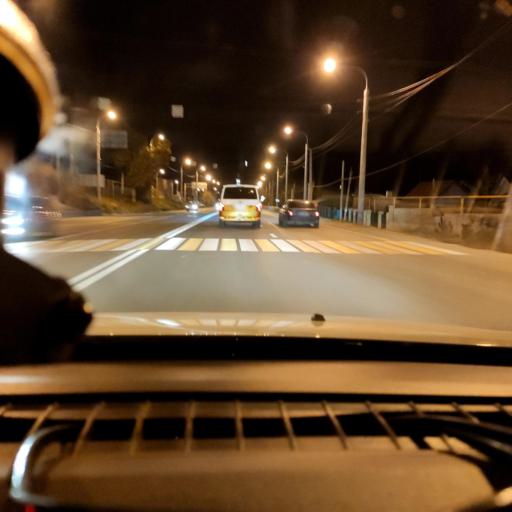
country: RU
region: Samara
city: Volzhskiy
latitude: 53.4312
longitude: 50.1180
